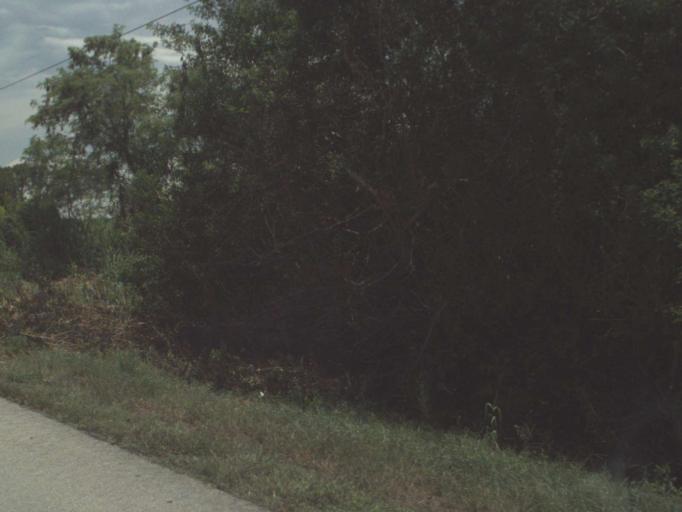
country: US
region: Florida
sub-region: Martin County
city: Indiantown
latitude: 27.0129
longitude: -80.6270
